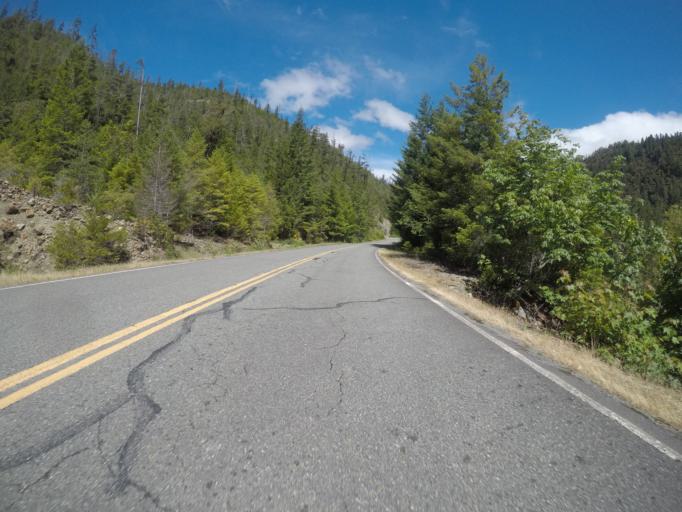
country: US
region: California
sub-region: Del Norte County
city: Bertsch-Oceanview
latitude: 41.7051
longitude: -123.9393
